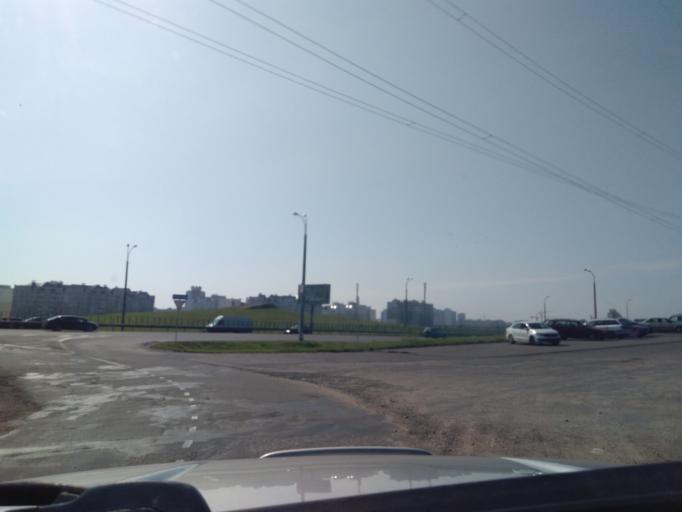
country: BY
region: Minsk
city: Zhdanovichy
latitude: 53.9289
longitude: 27.4190
